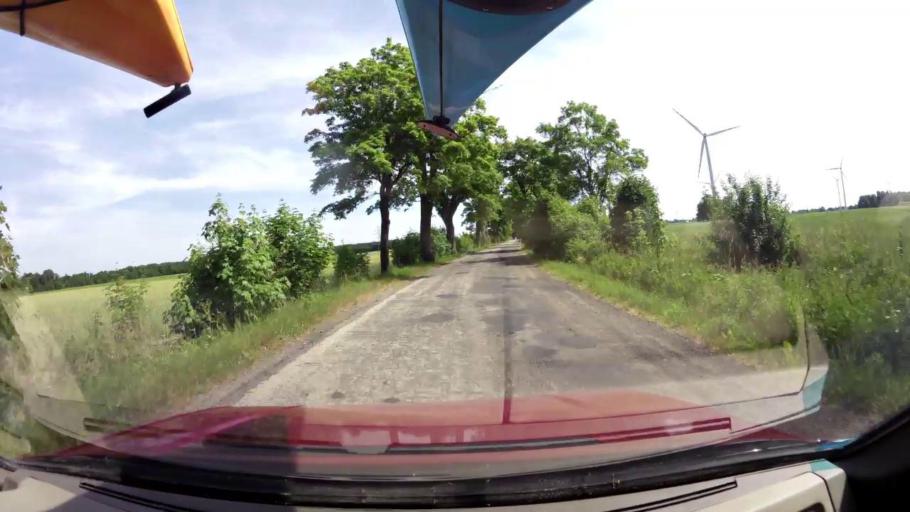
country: PL
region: West Pomeranian Voivodeship
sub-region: Powiat koszalinski
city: Sianow
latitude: 54.3185
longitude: 16.3220
